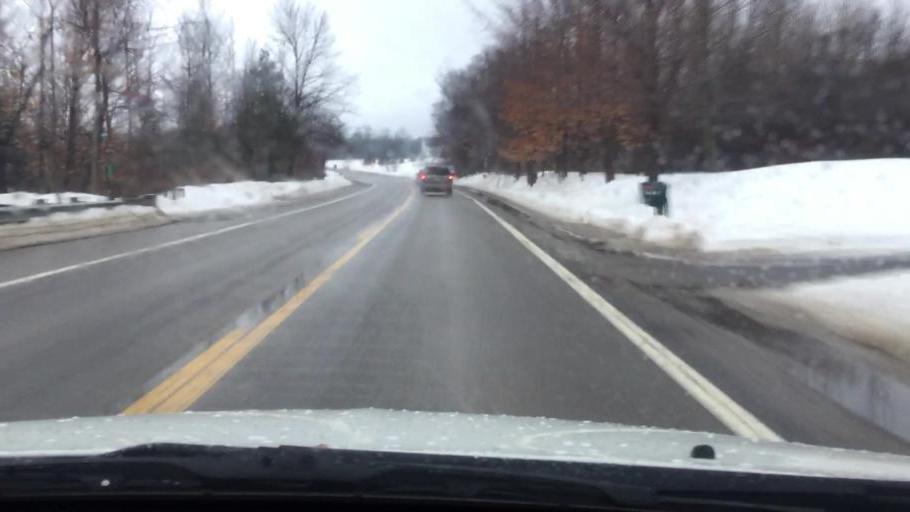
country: US
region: Michigan
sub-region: Charlevoix County
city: East Jordan
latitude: 45.1990
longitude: -85.1652
